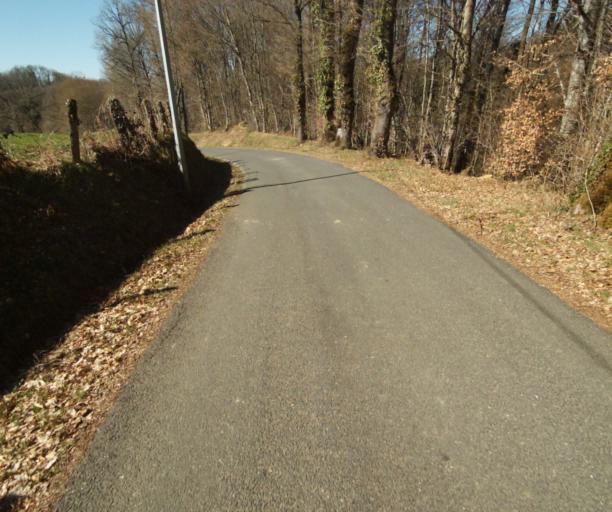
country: FR
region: Limousin
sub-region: Departement de la Correze
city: Chamboulive
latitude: 45.4027
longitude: 1.6417
